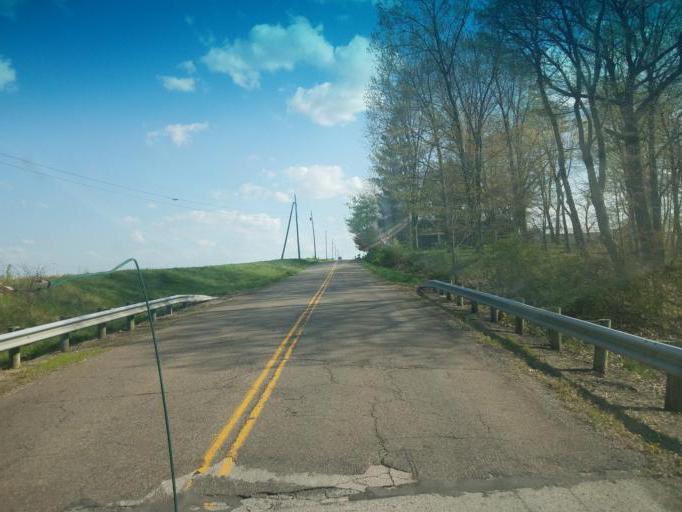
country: US
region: Ohio
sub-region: Wayne County
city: Smithville
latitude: 40.8623
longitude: -81.8780
